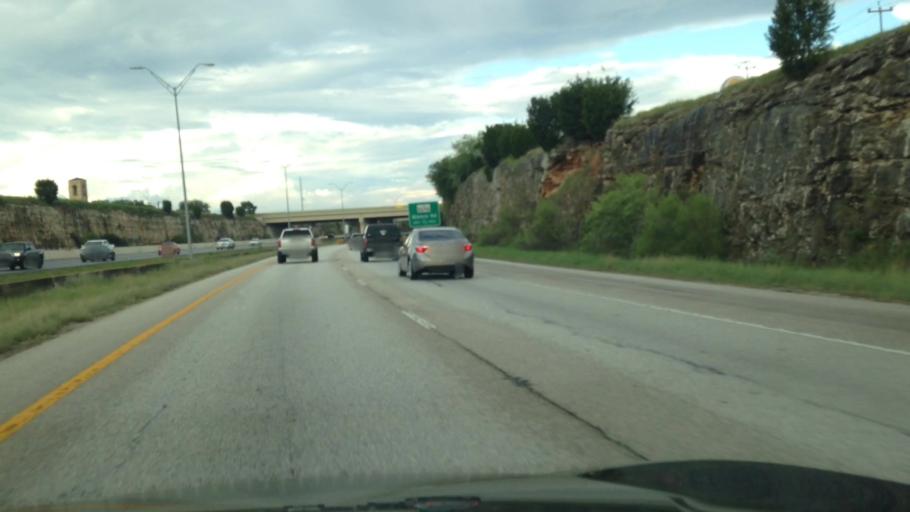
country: US
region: Texas
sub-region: Bexar County
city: Shavano Park
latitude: 29.6073
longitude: -98.5257
